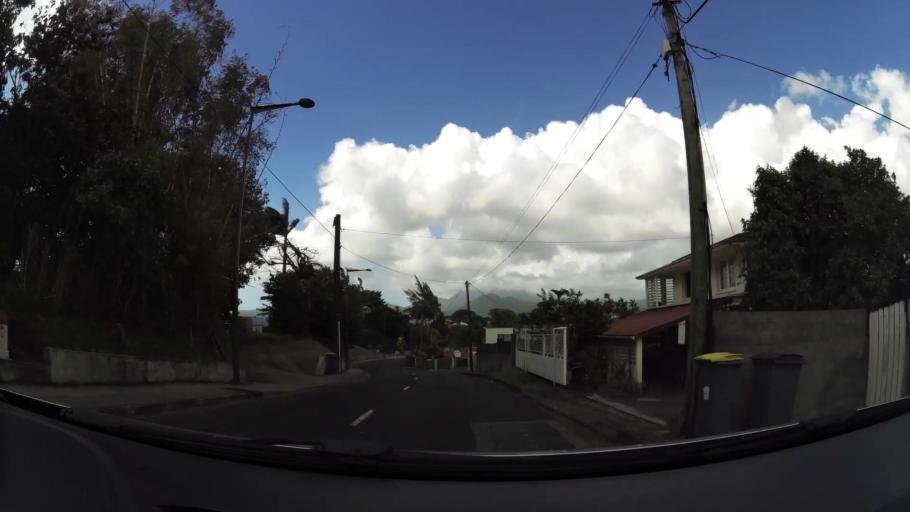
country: MQ
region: Martinique
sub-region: Martinique
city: Fort-de-France
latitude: 14.6344
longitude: -61.0546
